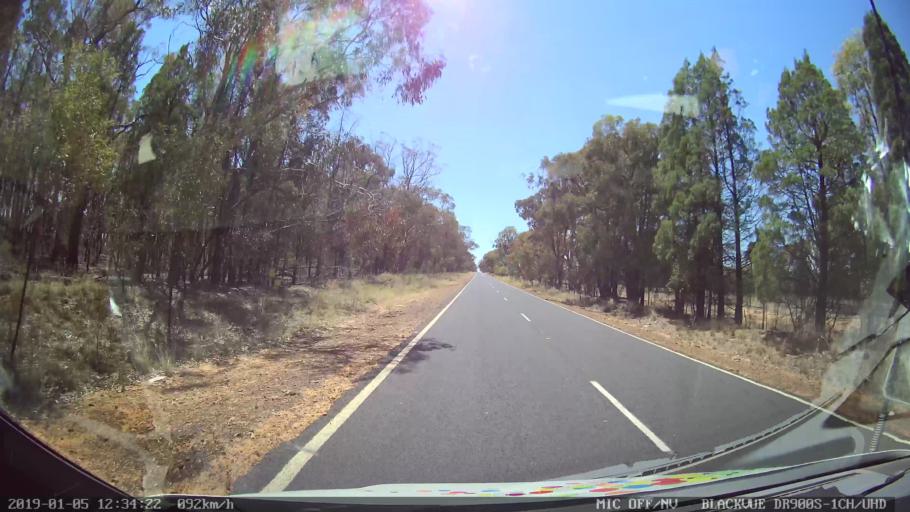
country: AU
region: New South Wales
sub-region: Warrumbungle Shire
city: Coonabarabran
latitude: -31.2123
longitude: 149.4093
